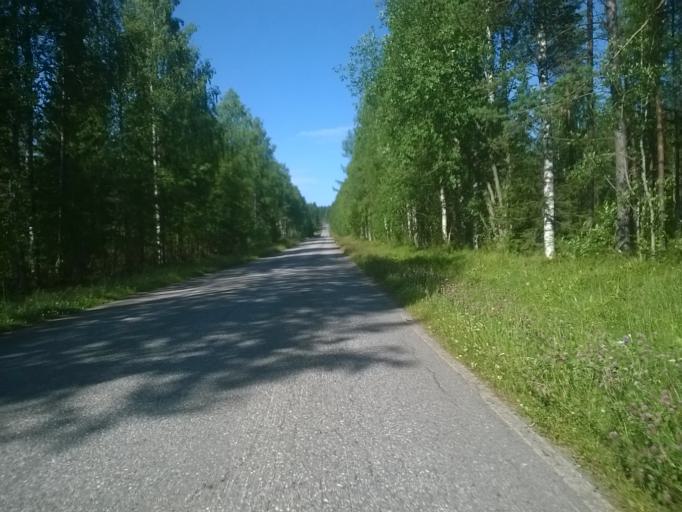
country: FI
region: Kainuu
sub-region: Kehys-Kainuu
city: Kuhmo
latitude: 64.1303
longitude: 29.4477
